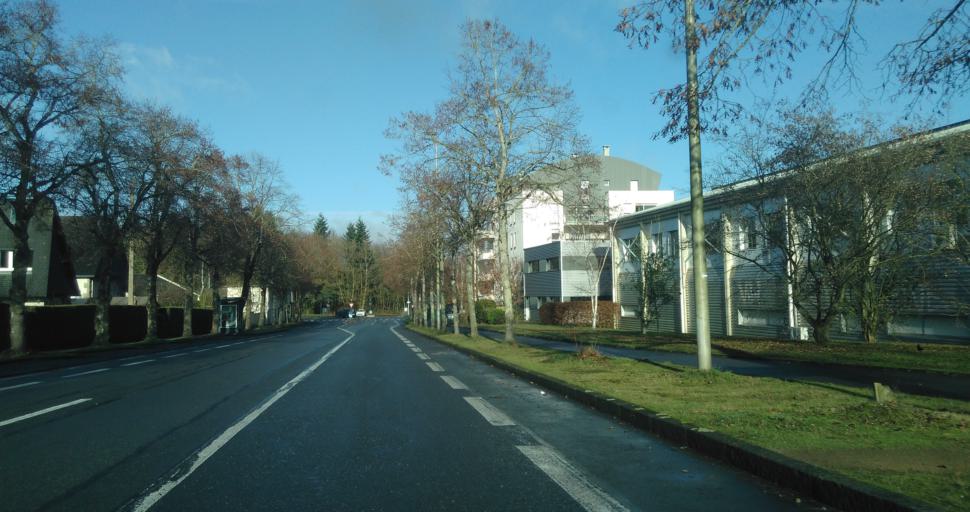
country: FR
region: Brittany
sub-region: Departement d'Ille-et-Vilaine
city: Rennes
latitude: 48.1284
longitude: -1.6422
